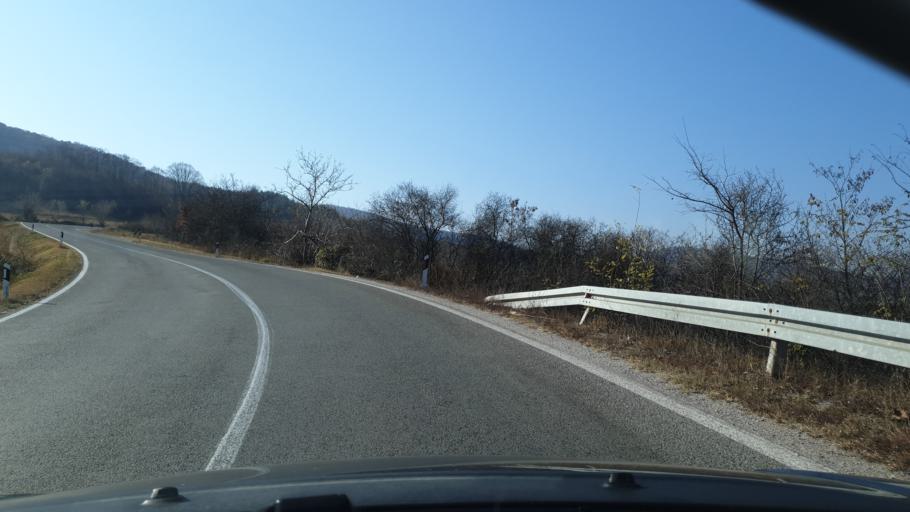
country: RS
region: Central Serbia
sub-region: Nisavski Okrug
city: Svrljig
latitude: 43.3952
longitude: 22.0610
